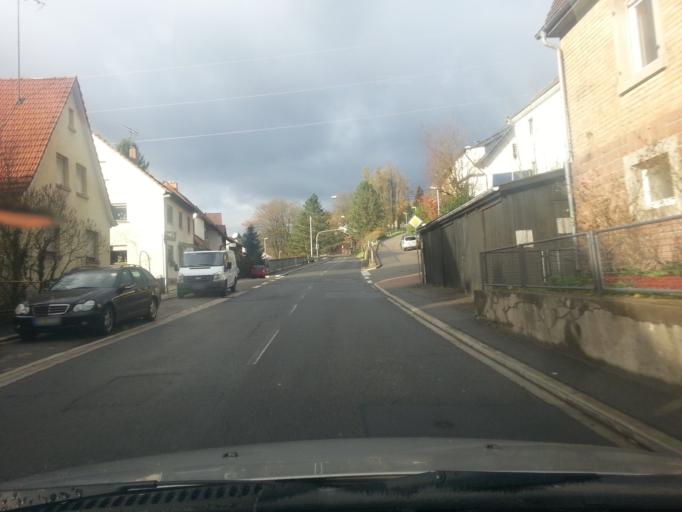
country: DE
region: Baden-Wuerttemberg
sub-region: Karlsruhe Region
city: Gaiberg
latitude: 49.3456
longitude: 8.7530
